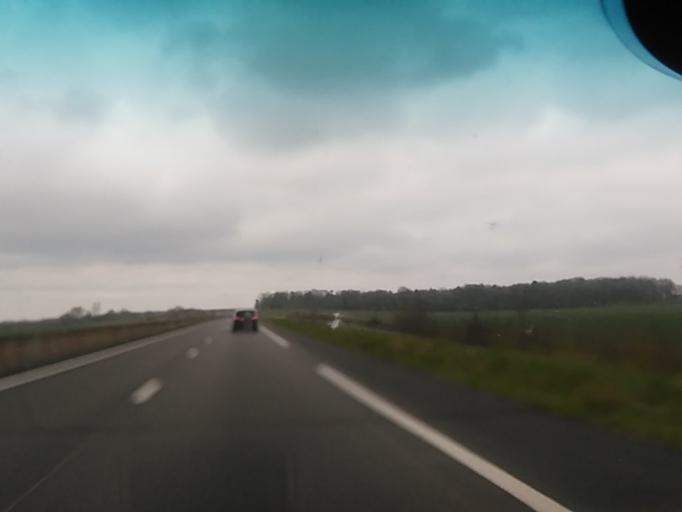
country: FR
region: Lower Normandy
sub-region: Departement du Calvados
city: Orbec
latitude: 48.9143
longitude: 0.4041
